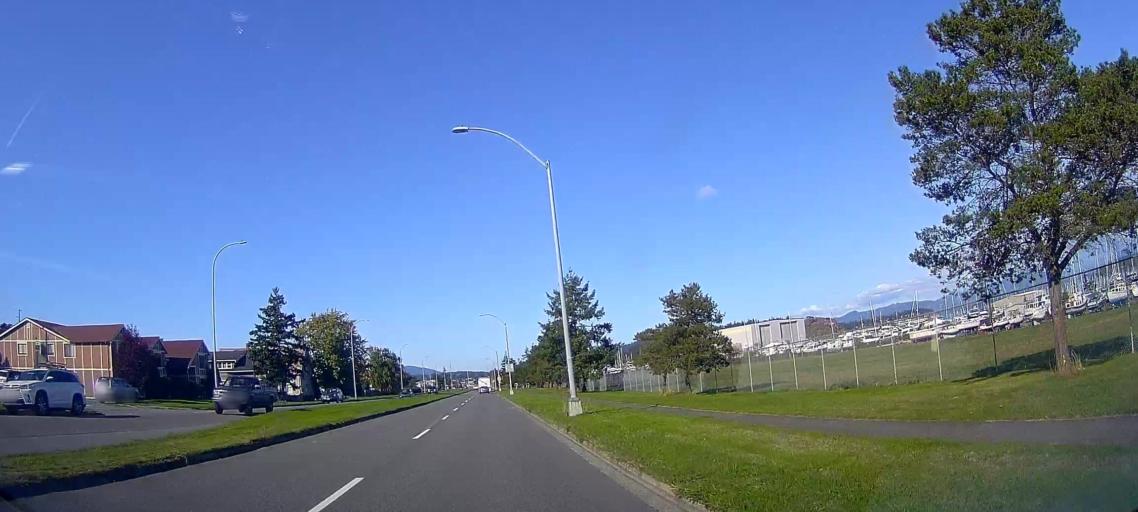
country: US
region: Washington
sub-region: Skagit County
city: Anacortes
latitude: 48.5002
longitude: -122.6095
